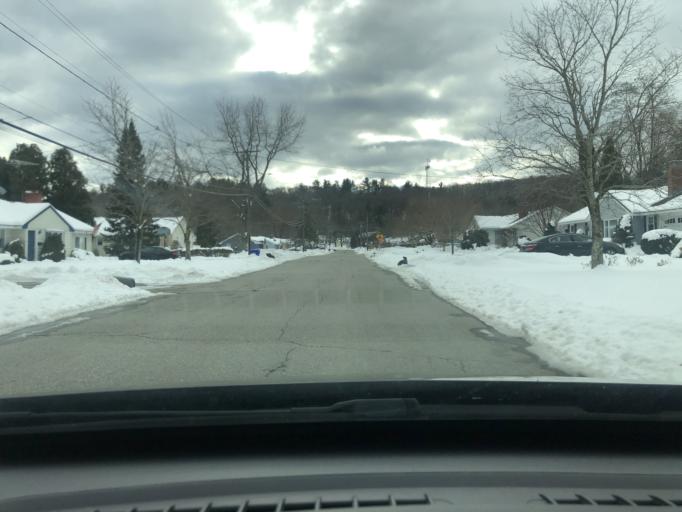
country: US
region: Massachusetts
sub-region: Middlesex County
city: Maynard
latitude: 42.4390
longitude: -71.4666
